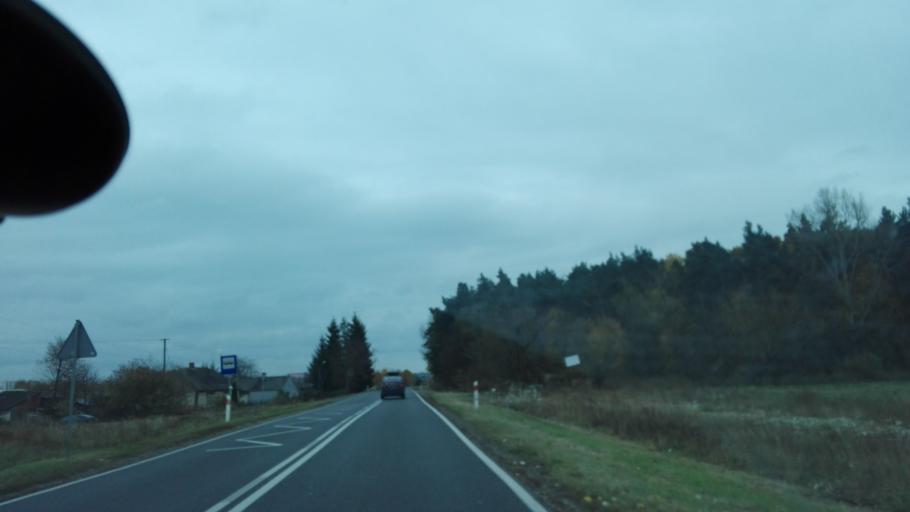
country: PL
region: Lublin Voivodeship
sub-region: Powiat pulawski
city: Pulawy
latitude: 51.4283
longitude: 21.9184
